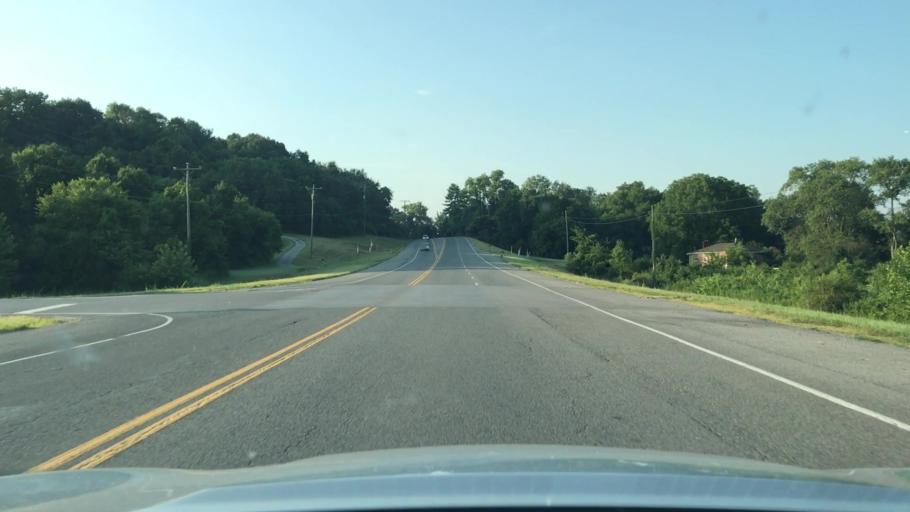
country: US
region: Tennessee
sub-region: Williamson County
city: Nolensville
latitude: 36.0078
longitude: -86.7010
